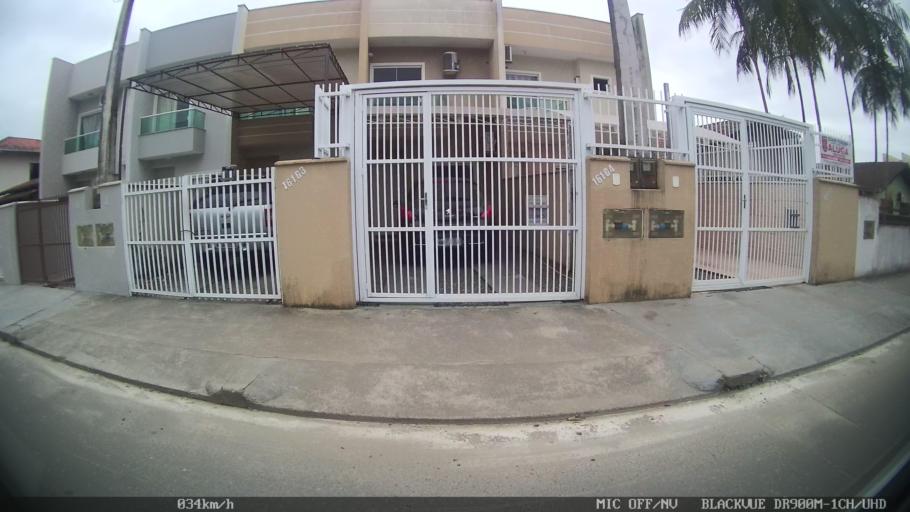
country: BR
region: Santa Catarina
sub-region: Joinville
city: Joinville
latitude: -26.3593
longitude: -48.8284
